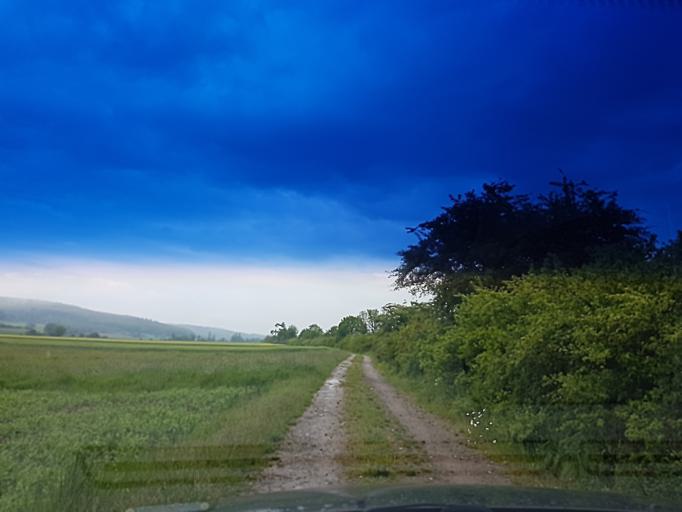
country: DE
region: Bavaria
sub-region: Upper Franconia
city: Zapfendorf
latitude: 50.0261
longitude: 10.9144
